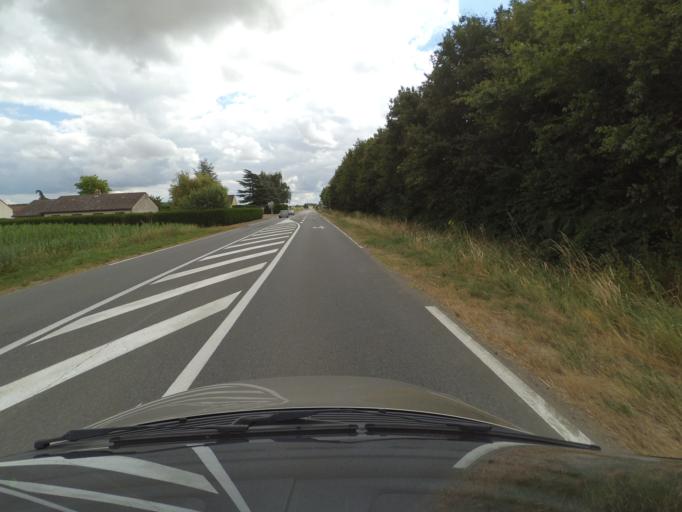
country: FR
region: Centre
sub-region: Departement d'Indre-et-Loire
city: Richelieu
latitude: 46.9717
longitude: 0.3676
